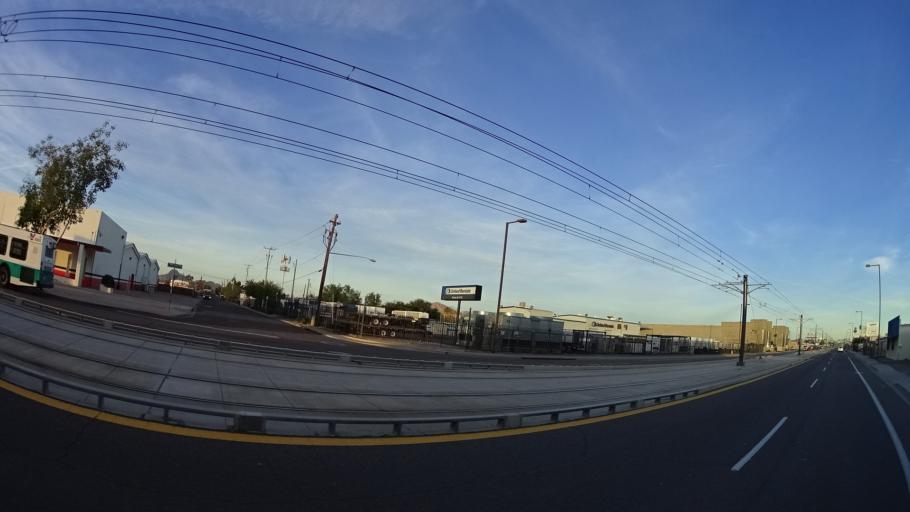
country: US
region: Arizona
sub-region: Maricopa County
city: Phoenix
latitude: 33.4481
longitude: -112.0114
